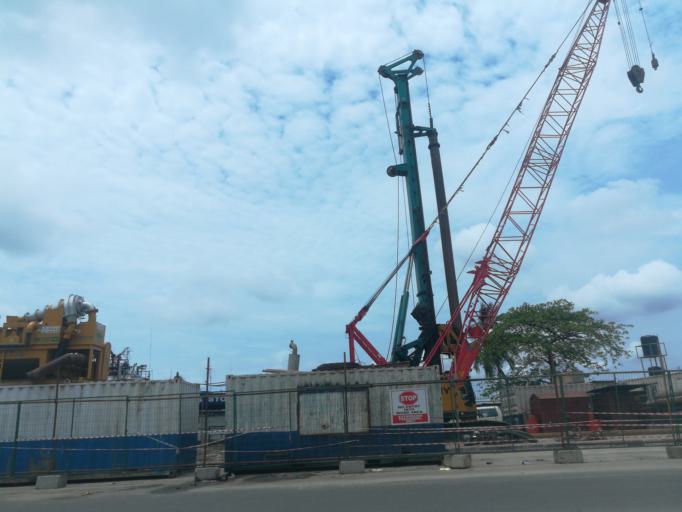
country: NG
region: Lagos
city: Lagos
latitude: 6.4554
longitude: 3.3811
